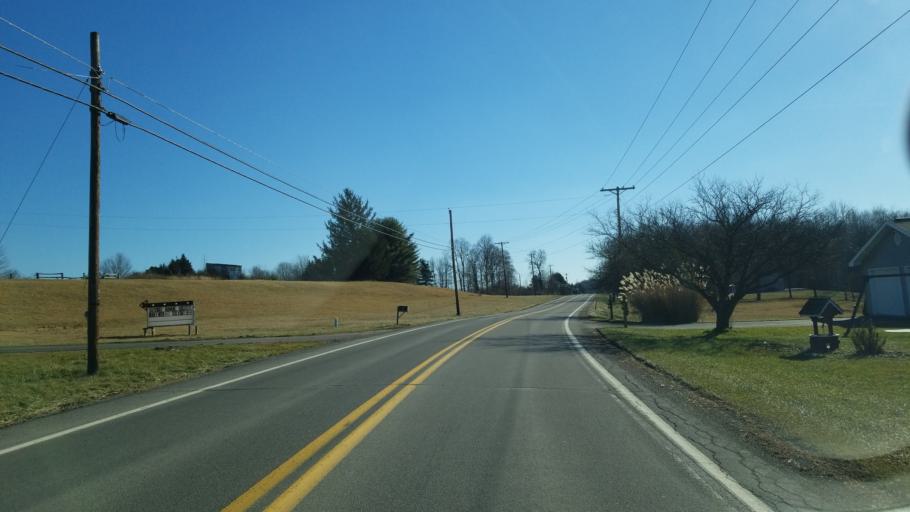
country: US
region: Pennsylvania
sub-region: Jefferson County
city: Falls Creek
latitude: 41.1631
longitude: -78.8263
